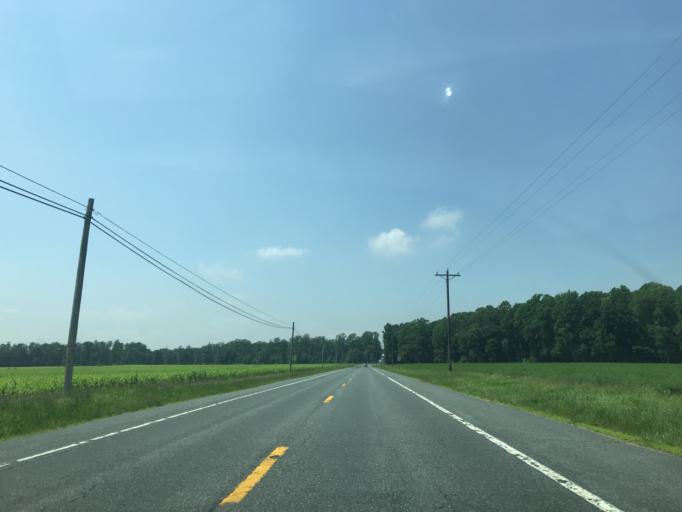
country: US
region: Maryland
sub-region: Caroline County
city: Federalsburg
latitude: 38.6598
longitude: -75.7318
